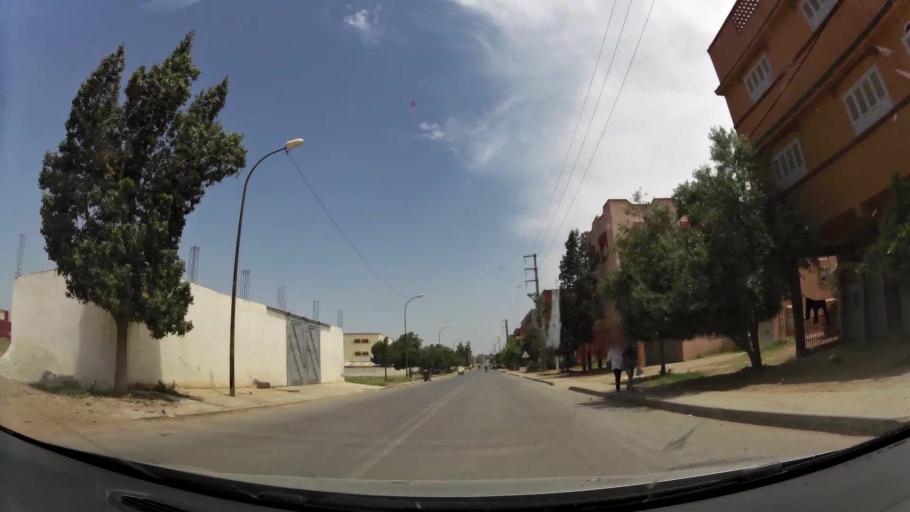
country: MA
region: Rabat-Sale-Zemmour-Zaer
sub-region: Khemisset
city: Khemisset
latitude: 33.8210
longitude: -6.0791
